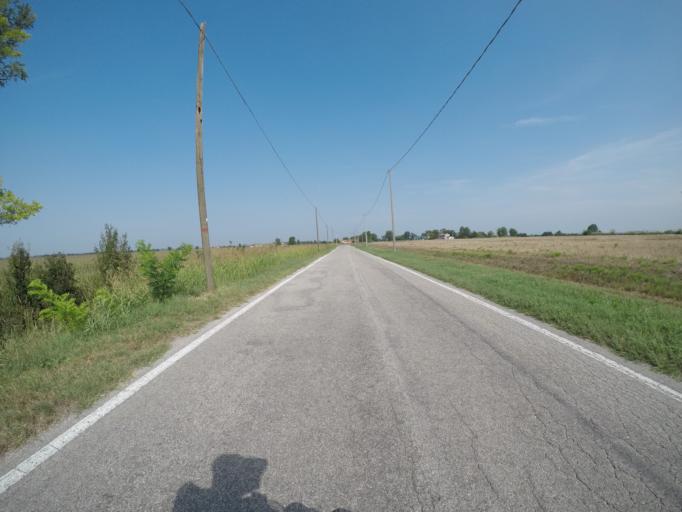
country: IT
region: Veneto
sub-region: Provincia di Rovigo
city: Villanova del Ghebbo Canton
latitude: 45.0567
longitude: 11.6287
